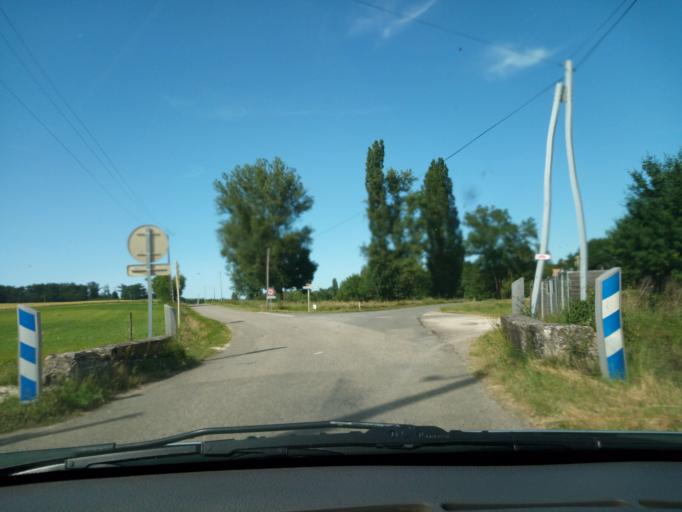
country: FR
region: Midi-Pyrenees
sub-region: Departement du Tarn-et-Garonne
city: Molieres
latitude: 44.2192
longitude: 1.3256
